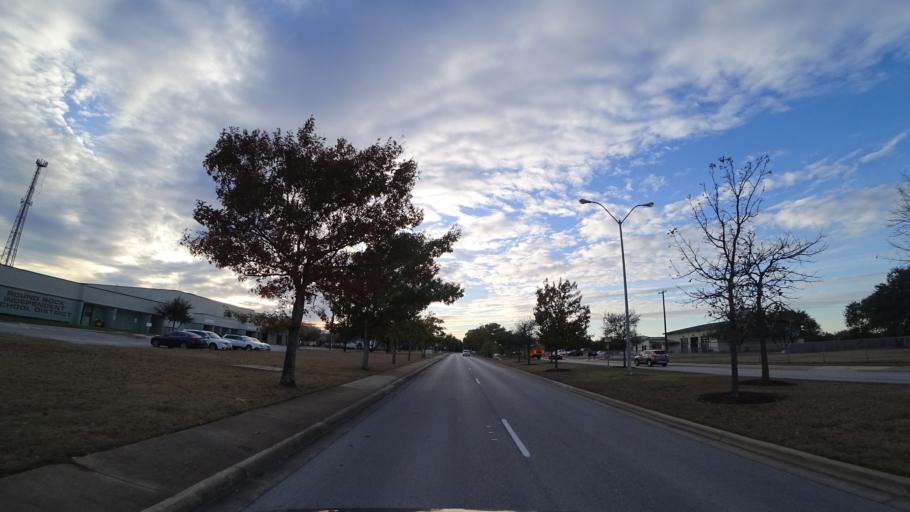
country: US
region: Texas
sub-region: Williamson County
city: Brushy Creek
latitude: 30.4950
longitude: -97.7332
